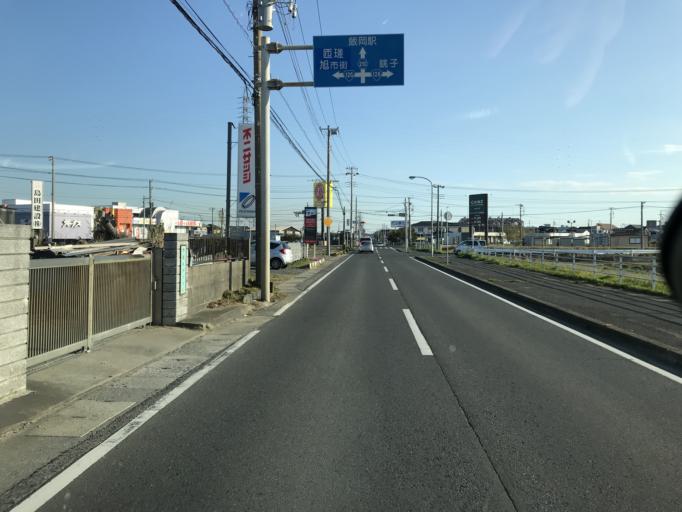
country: JP
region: Chiba
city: Asahi
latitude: 35.7207
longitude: 140.6840
